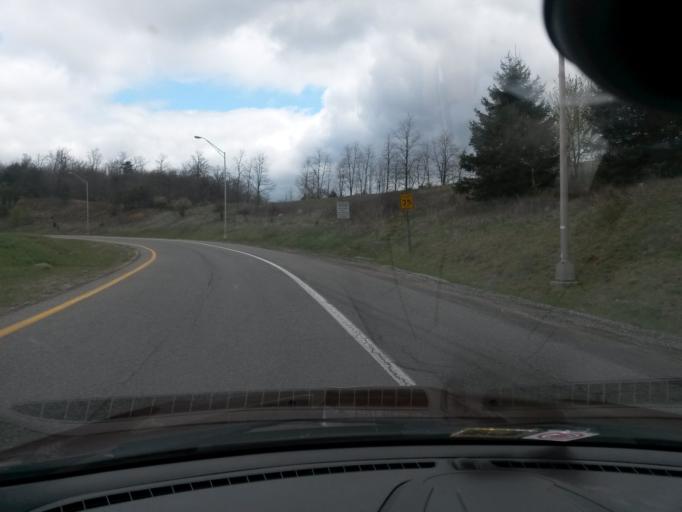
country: US
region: Virginia
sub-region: Montgomery County
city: Christiansburg
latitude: 37.1270
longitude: -80.3689
